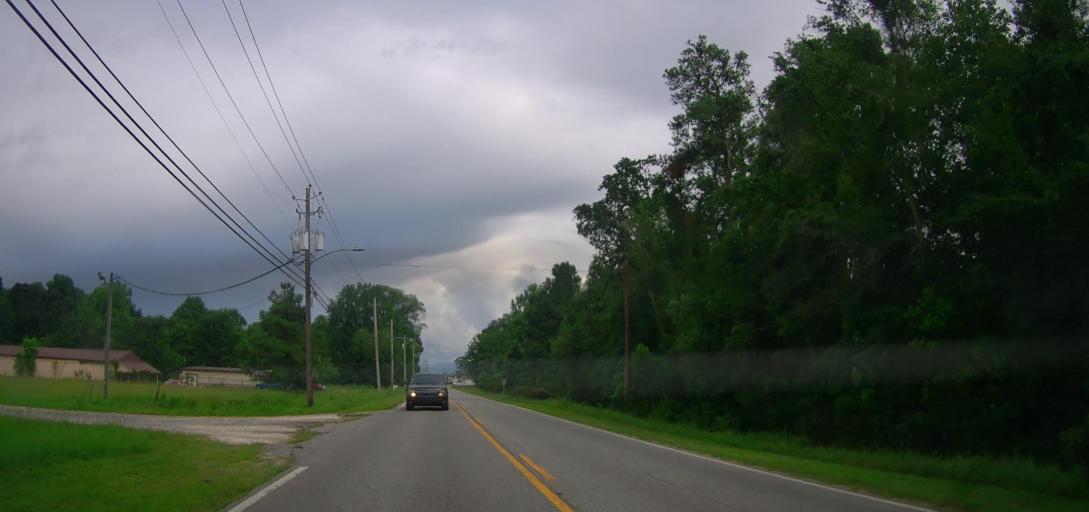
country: US
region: Georgia
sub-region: Wayne County
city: Jesup
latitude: 31.6138
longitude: -81.8934
